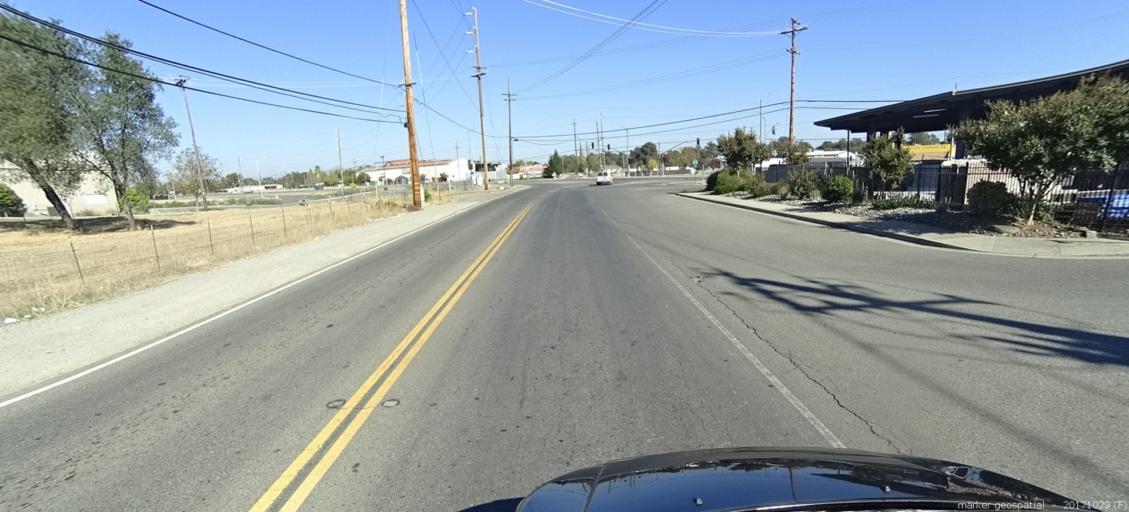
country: US
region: California
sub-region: Shasta County
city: Redding
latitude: 40.5160
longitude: -122.3824
